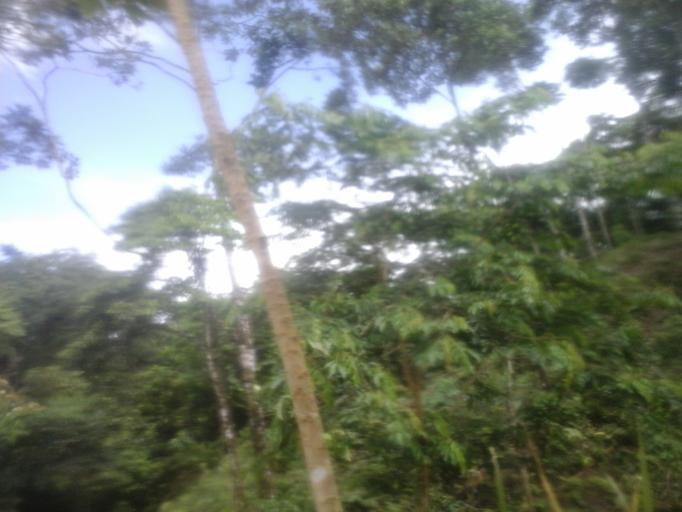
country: CO
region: Putumayo
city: Orito
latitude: 0.6471
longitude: -76.8191
